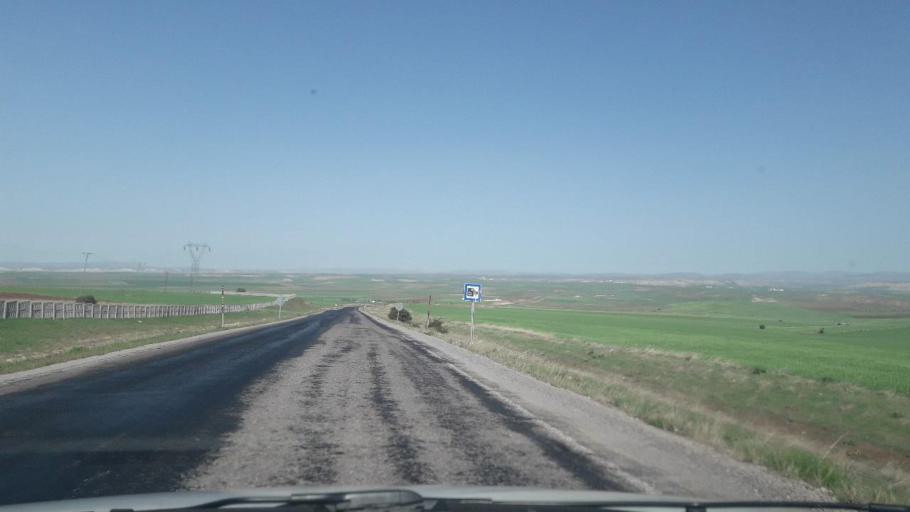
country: TR
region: Sivas
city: Kangal
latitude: 39.1709
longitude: 37.4643
